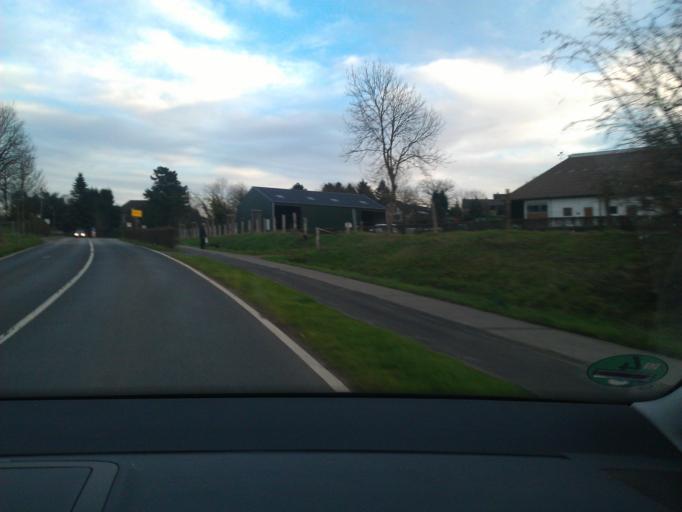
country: DE
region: North Rhine-Westphalia
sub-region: Regierungsbezirk Koln
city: Roetgen
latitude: 50.7103
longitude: 6.1737
